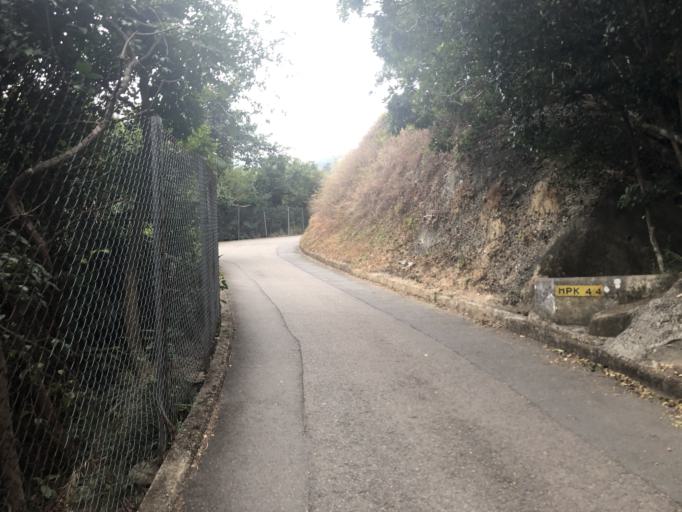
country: HK
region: Wanchai
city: Wan Chai
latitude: 22.2812
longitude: 114.2104
